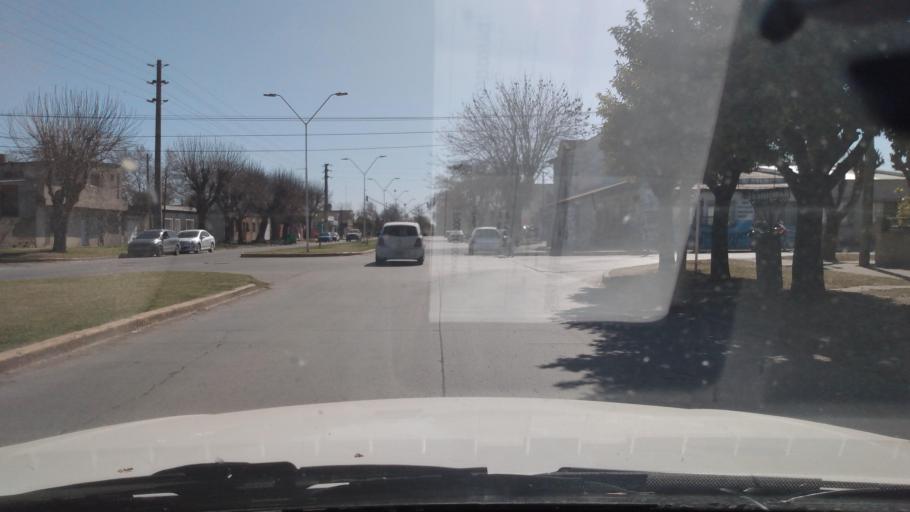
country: AR
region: Buenos Aires
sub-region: Partido de Mercedes
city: Mercedes
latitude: -34.6548
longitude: -59.4177
